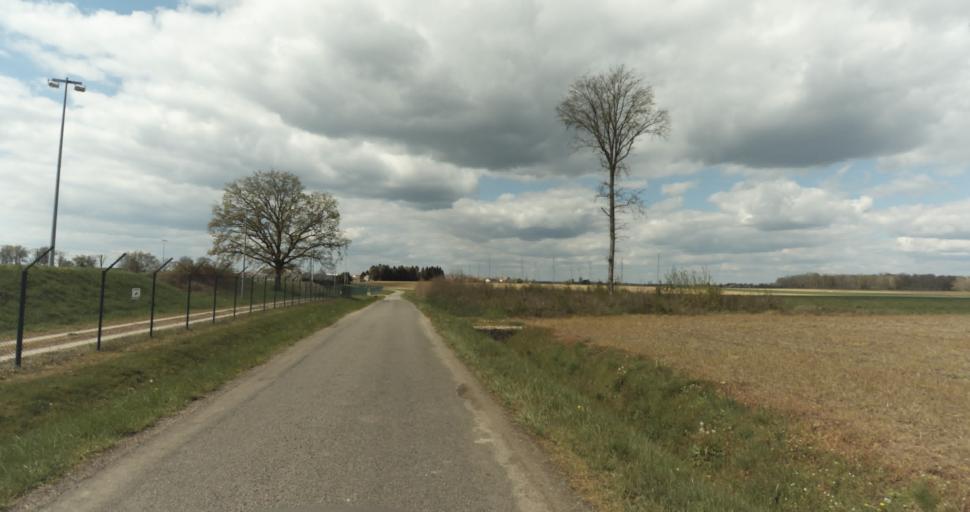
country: FR
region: Bourgogne
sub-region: Departement de la Cote-d'Or
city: Auxonne
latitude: 47.1761
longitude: 5.4107
